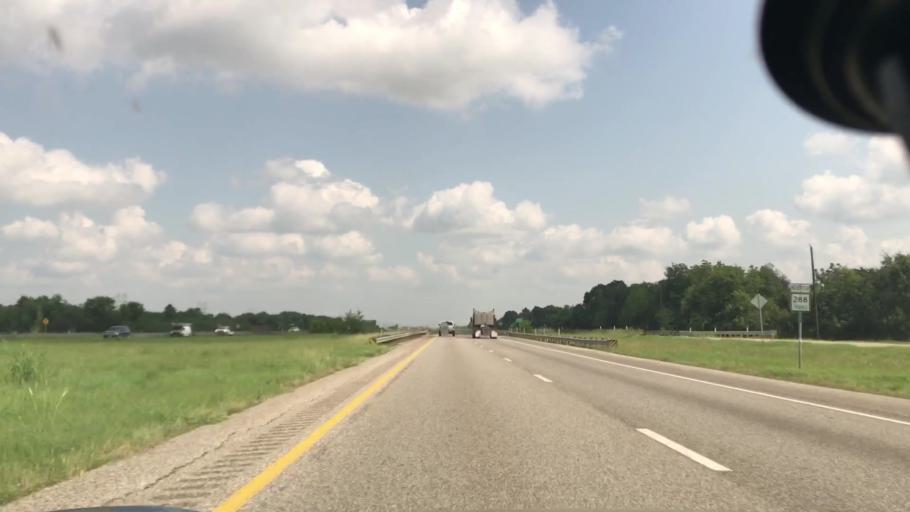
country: US
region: Texas
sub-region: Brazoria County
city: Rosharon
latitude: 29.3921
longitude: -95.4267
